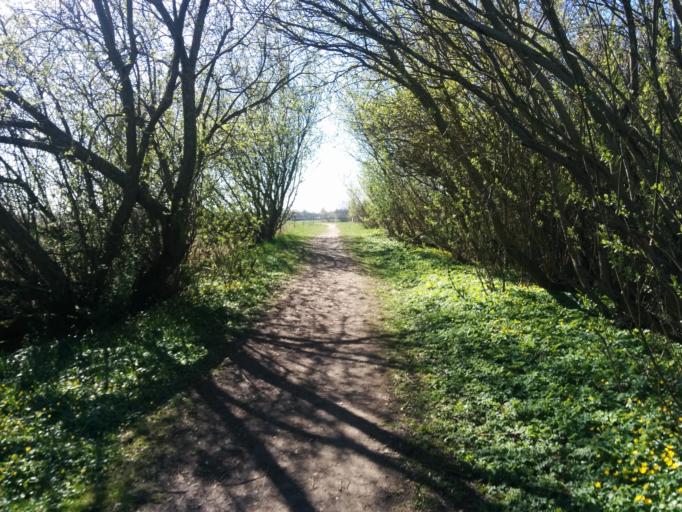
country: DK
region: North Denmark
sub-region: Alborg Kommune
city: Aalborg
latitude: 57.0163
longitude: 9.9151
